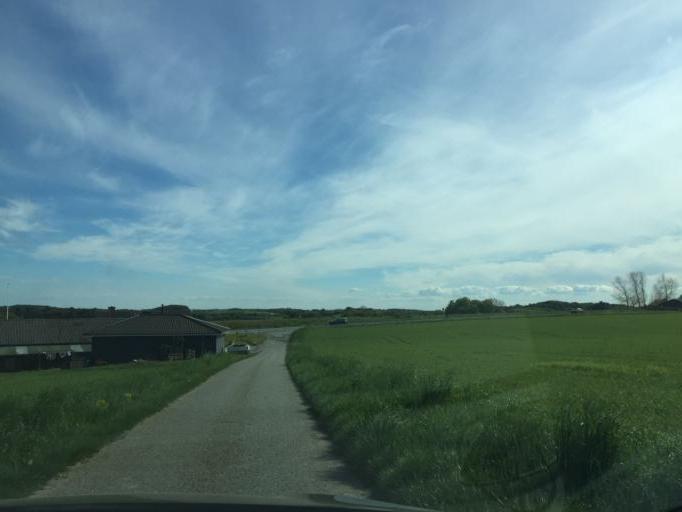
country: DK
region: South Denmark
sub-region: Fredericia Kommune
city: Taulov
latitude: 55.5299
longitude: 9.5651
